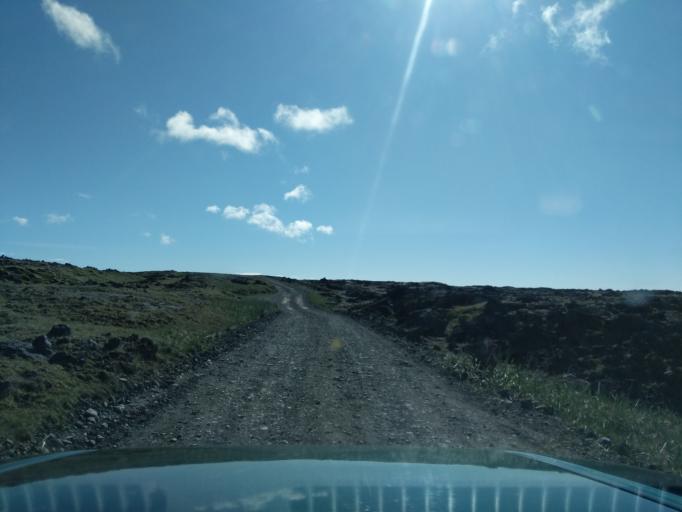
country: IS
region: West
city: Olafsvik
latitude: 64.8793
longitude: -23.9896
